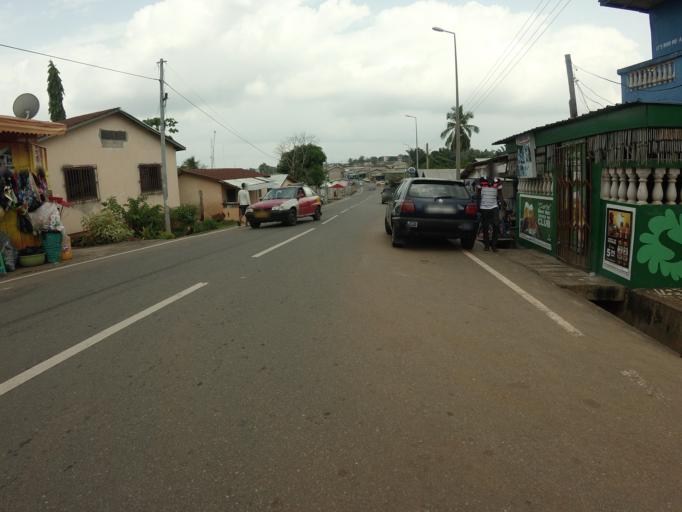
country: GH
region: Volta
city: Ho
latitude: 6.6162
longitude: 0.4664
